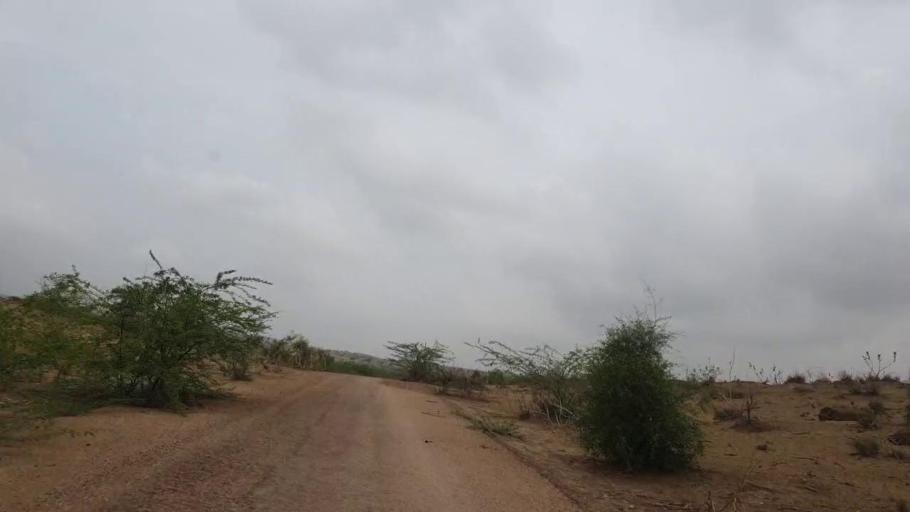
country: PK
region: Sindh
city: Diplo
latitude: 24.5207
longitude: 69.4694
